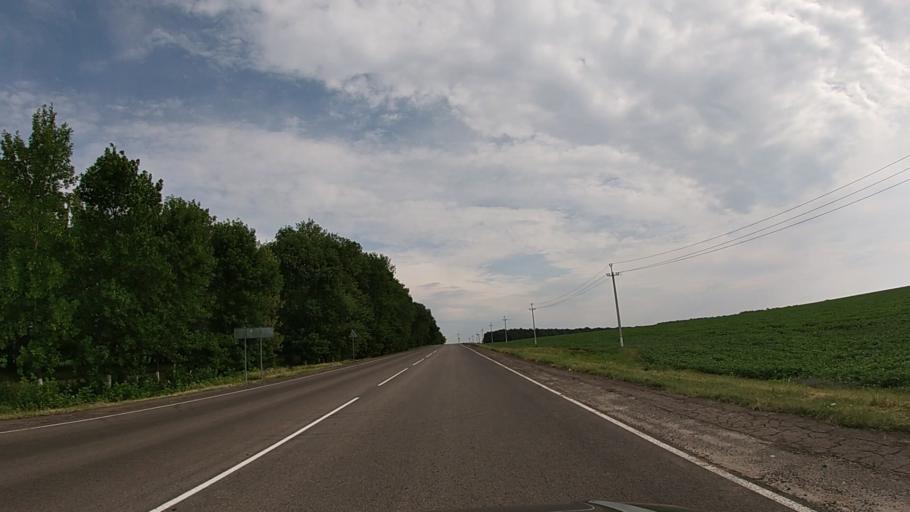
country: RU
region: Belgorod
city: Krasnaya Yaruga
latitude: 50.8102
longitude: 35.5002
